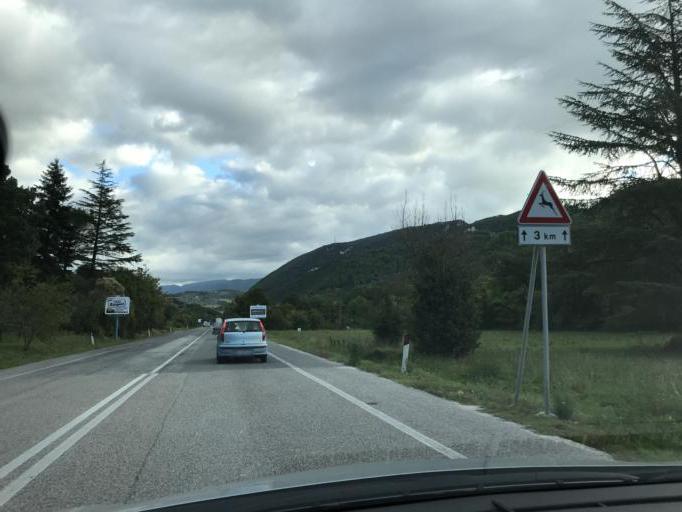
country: IT
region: Umbria
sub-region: Provincia di Perugia
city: Spoleto
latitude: 42.7146
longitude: 12.7221
